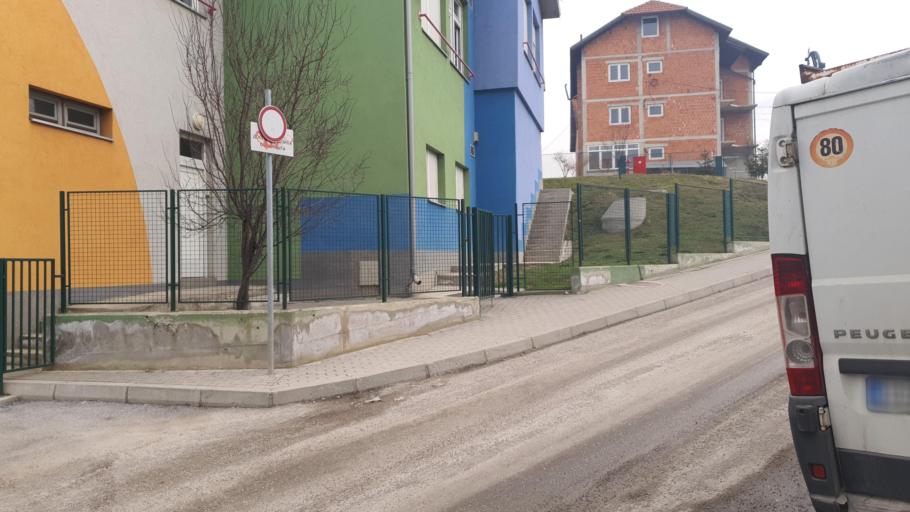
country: RS
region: Central Serbia
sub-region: Zlatiborski Okrug
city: Uzice
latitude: 43.8606
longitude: 19.8317
